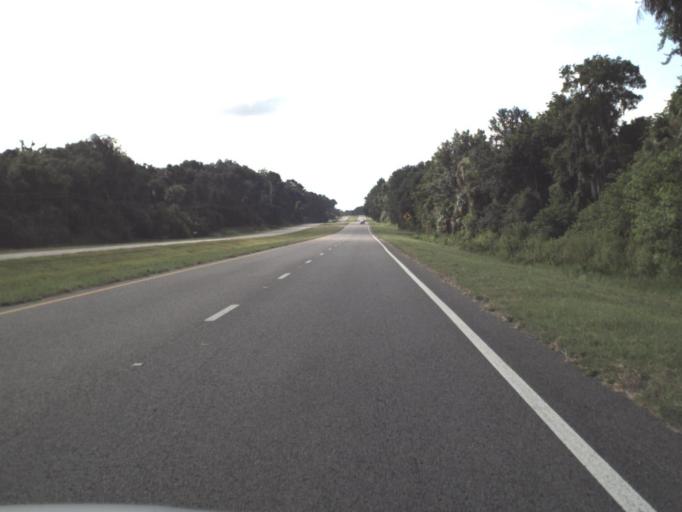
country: US
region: Florida
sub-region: Alachua County
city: Gainesville
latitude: 29.4970
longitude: -82.2595
